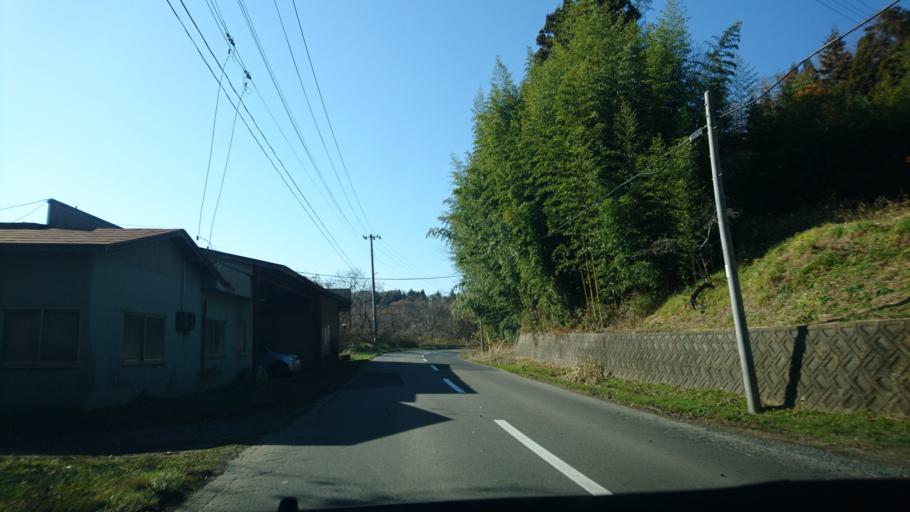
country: JP
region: Iwate
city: Ichinoseki
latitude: 38.9015
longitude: 141.3956
